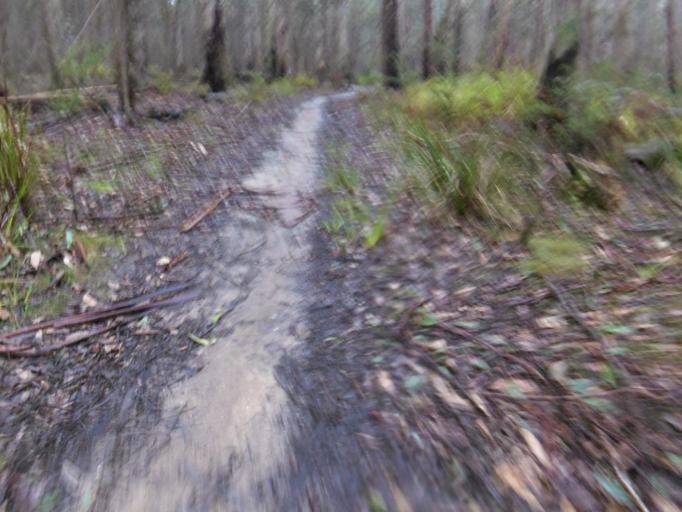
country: AU
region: Victoria
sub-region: Moorabool
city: Bacchus Marsh
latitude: -37.4186
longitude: 144.4836
